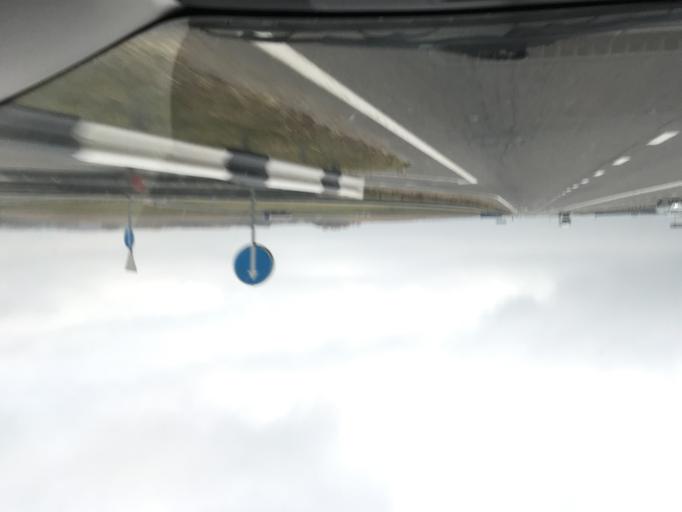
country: BY
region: Vitebsk
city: Vitebsk
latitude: 55.1539
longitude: 30.0659
